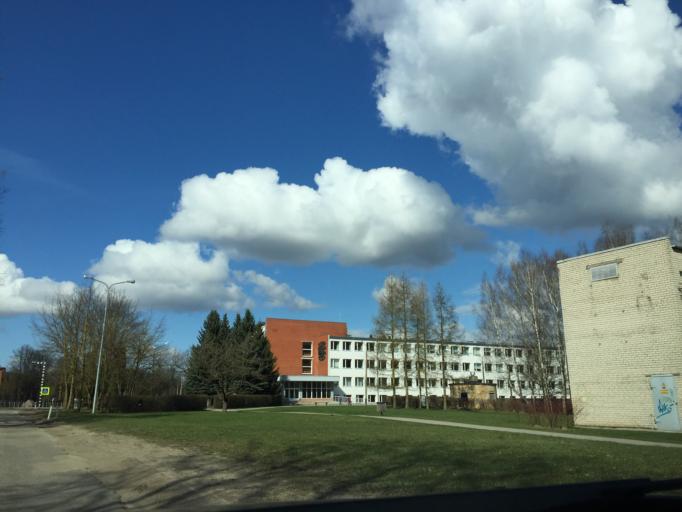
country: LV
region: Kekava
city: Kekava
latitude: 56.8257
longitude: 24.2295
